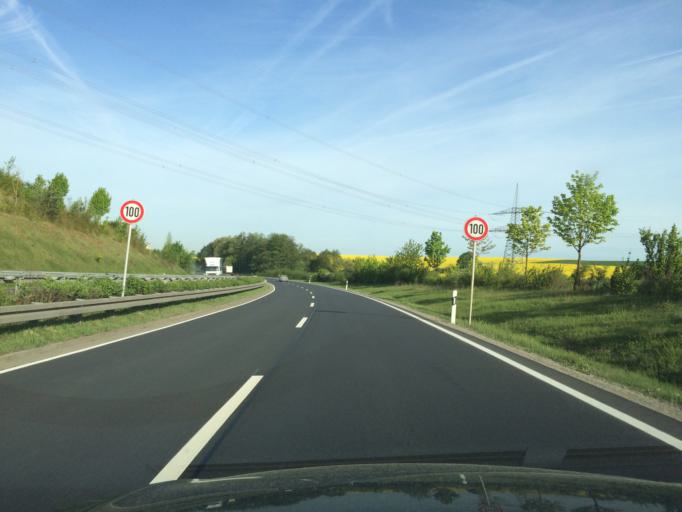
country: DE
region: Bavaria
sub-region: Regierungsbezirk Unterfranken
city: Rottendorf
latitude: 49.7809
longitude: 10.0504
